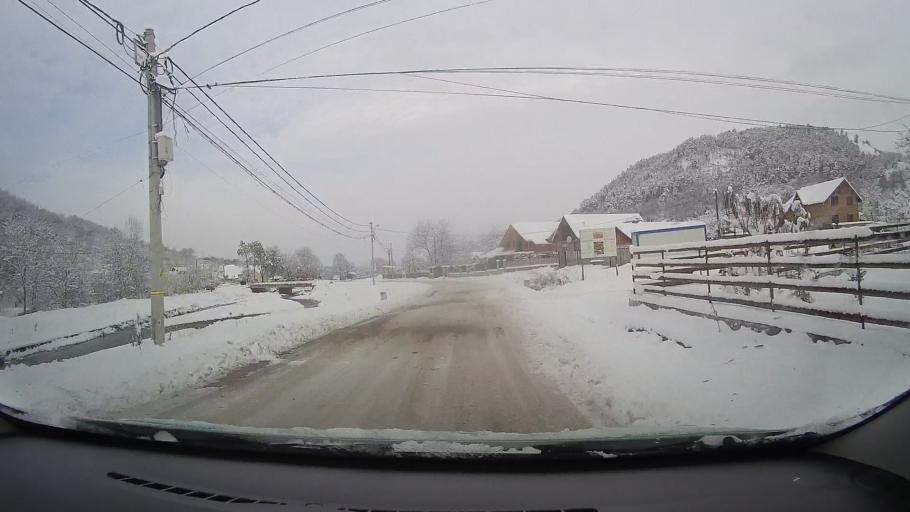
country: RO
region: Alba
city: Pianu de Sus
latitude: 45.8890
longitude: 23.4872
